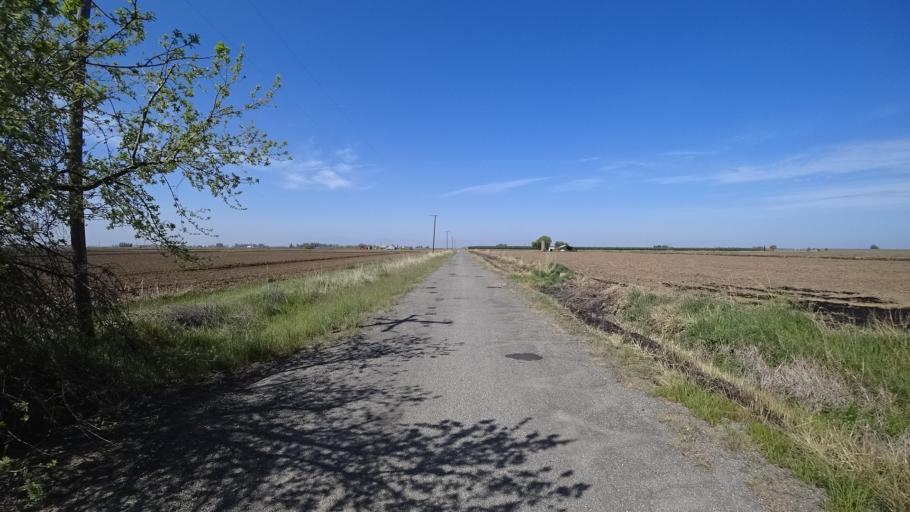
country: US
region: California
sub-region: Glenn County
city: Hamilton City
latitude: 39.6089
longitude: -122.0323
